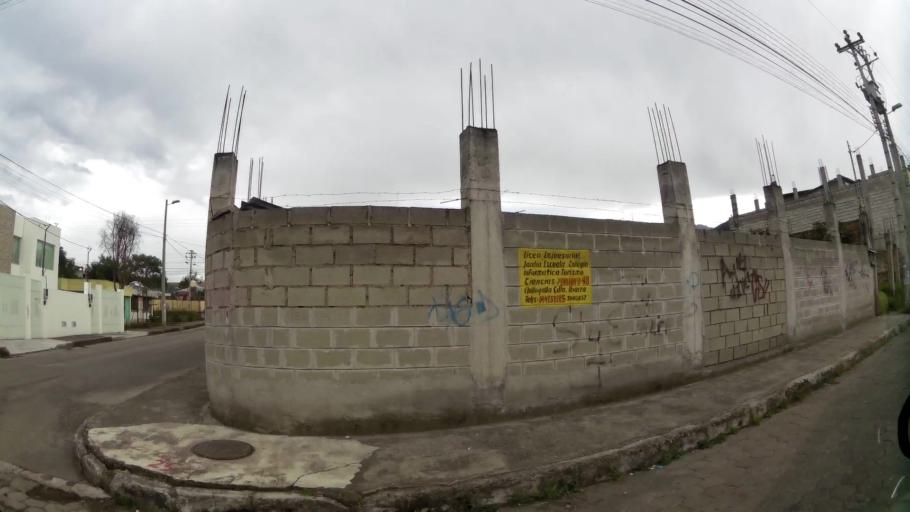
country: EC
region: Pichincha
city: Quito
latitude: -0.3097
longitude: -78.5530
